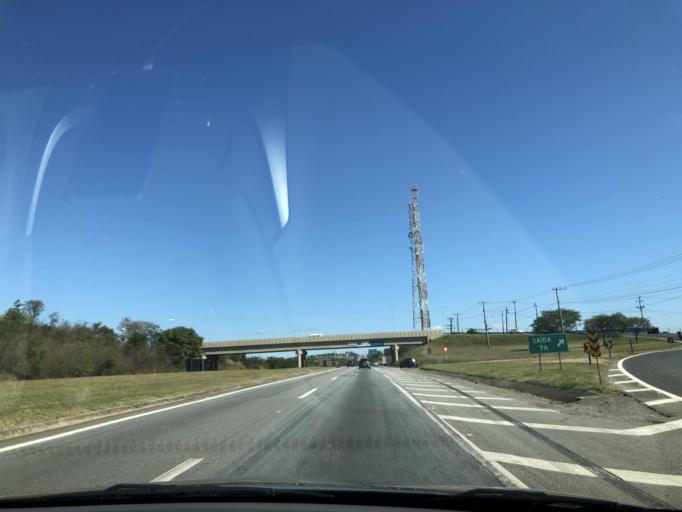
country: BR
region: Sao Paulo
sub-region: Sorocaba
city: Sorocaba
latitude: -23.4382
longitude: -47.3780
